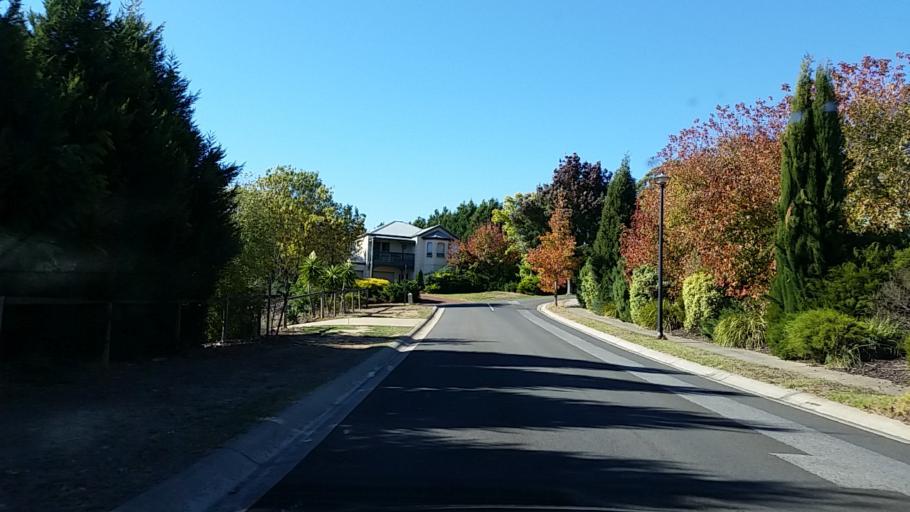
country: AU
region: South Australia
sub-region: Mount Barker
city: Mount Barker
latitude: -35.0612
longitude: 138.8779
